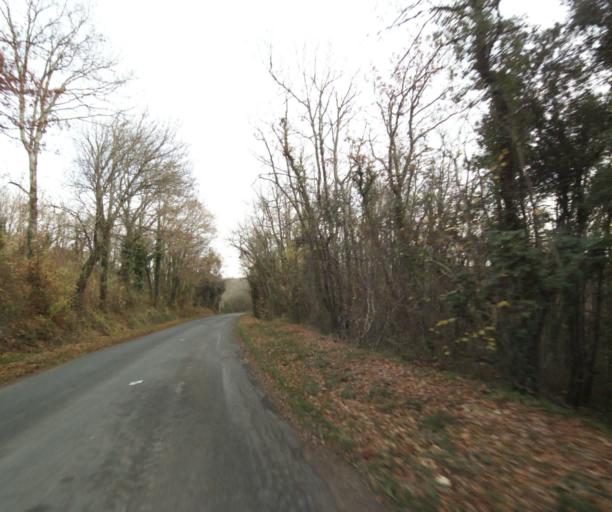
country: FR
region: Poitou-Charentes
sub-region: Departement de la Charente-Maritime
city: Bussac-sur-Charente
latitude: 45.8133
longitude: -0.6045
